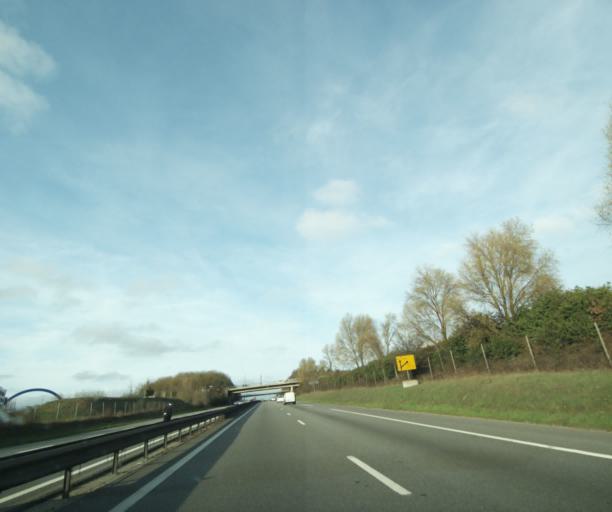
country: FR
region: Ile-de-France
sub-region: Departement des Yvelines
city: Bois-d'Arcy
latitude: 48.7870
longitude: 2.0361
